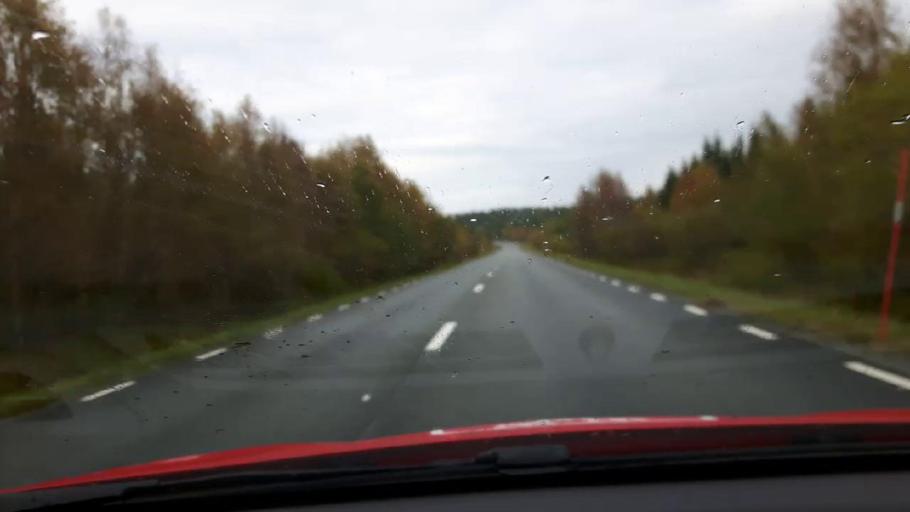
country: SE
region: Jaemtland
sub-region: Krokoms Kommun
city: Krokom
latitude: 63.0891
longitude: 14.2988
